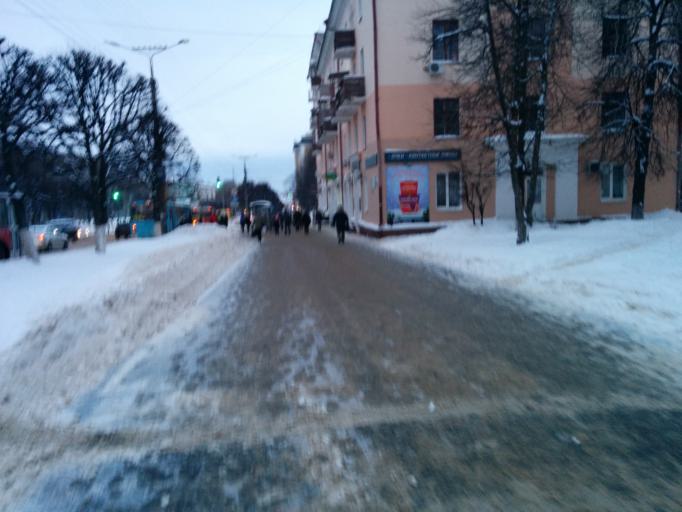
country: RU
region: Chuvashia
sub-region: Cheboksarskiy Rayon
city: Cheboksary
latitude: 56.1280
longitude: 47.2497
